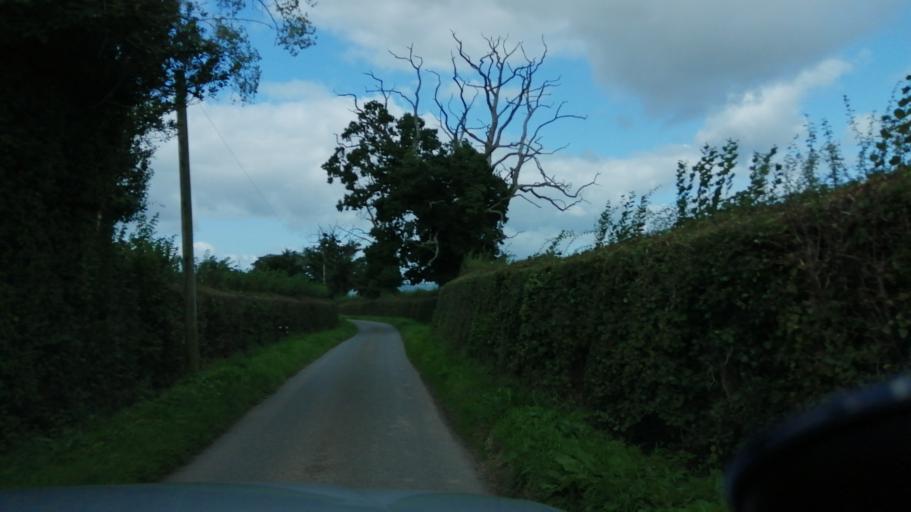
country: GB
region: England
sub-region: Herefordshire
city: Kinnersley
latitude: 52.1227
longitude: -2.9106
